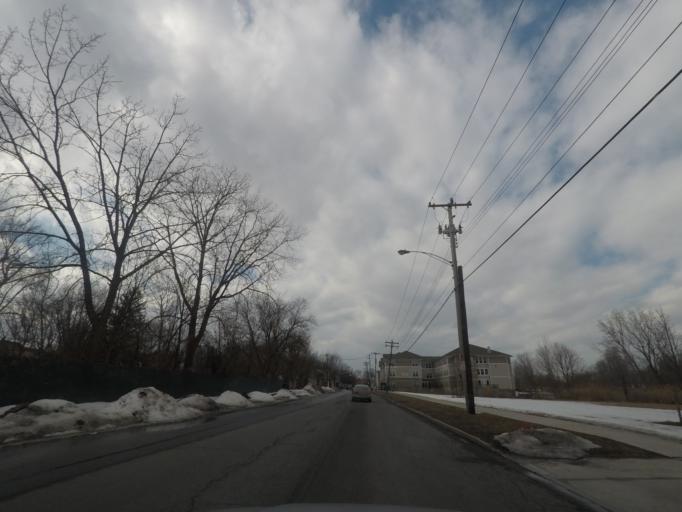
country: US
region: New York
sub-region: Albany County
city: West Albany
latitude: 42.6703
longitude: -73.7699
